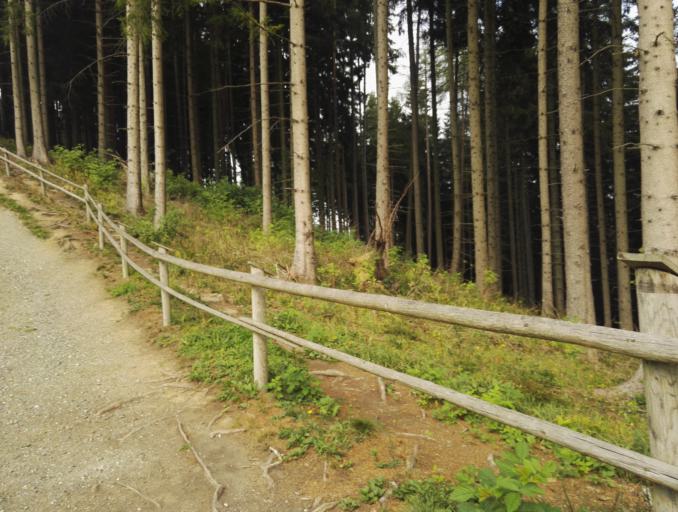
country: AT
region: Styria
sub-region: Politischer Bezirk Murtal
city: Sankt Margarethen bei Knittelfeld
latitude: 47.2165
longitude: 14.8741
